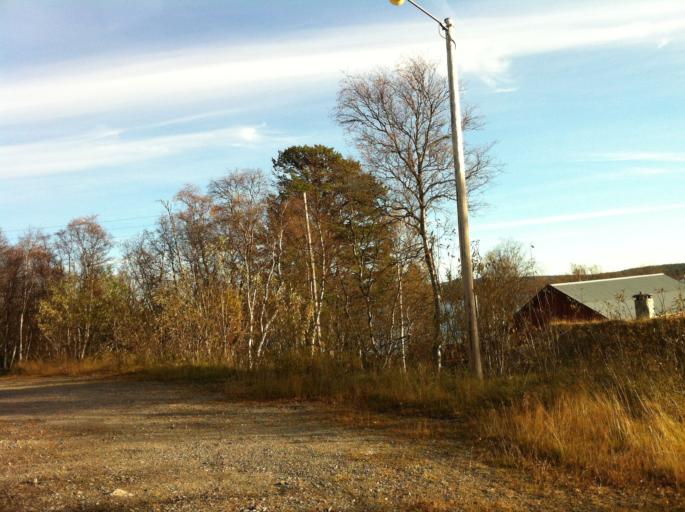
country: NO
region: Hedmark
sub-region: Engerdal
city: Engerdal
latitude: 62.0861
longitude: 12.0615
